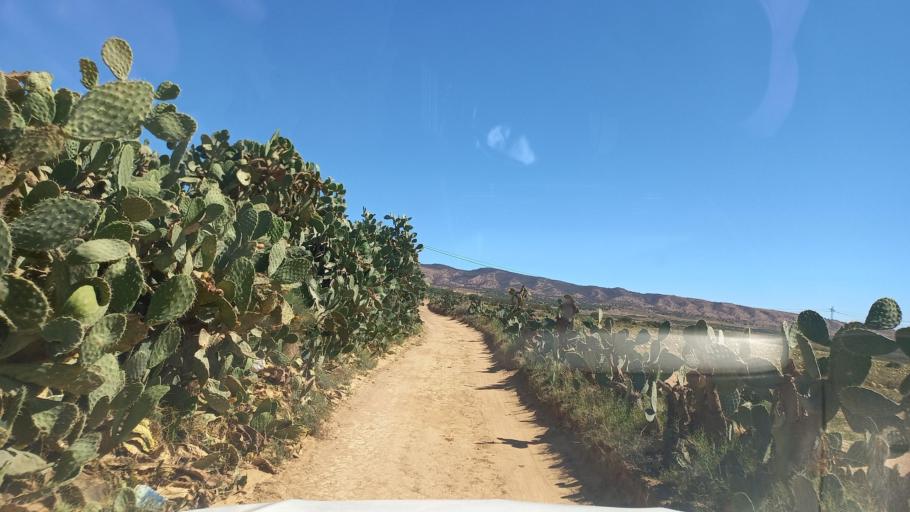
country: TN
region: Al Qasrayn
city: Sbiba
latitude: 35.3510
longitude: 9.1029
